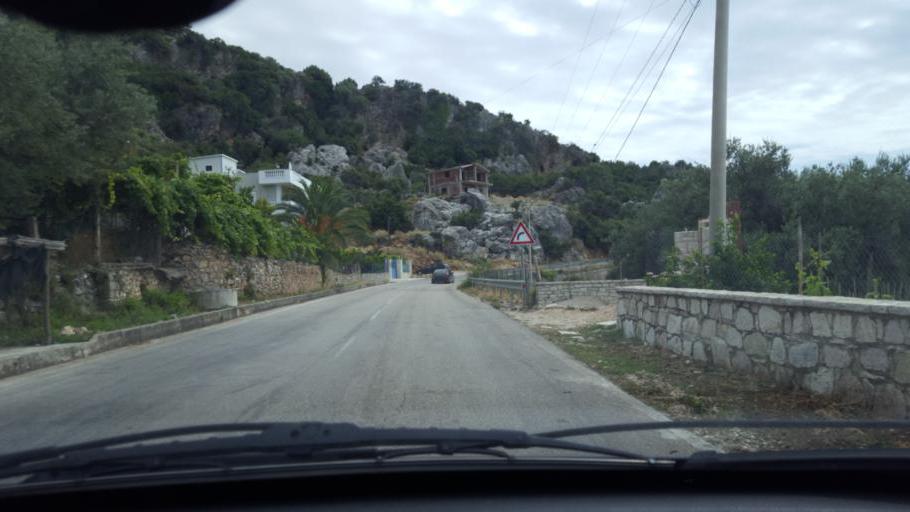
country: AL
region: Vlore
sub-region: Rrethi i Sarandes
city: Lukove
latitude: 40.0502
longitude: 19.8710
